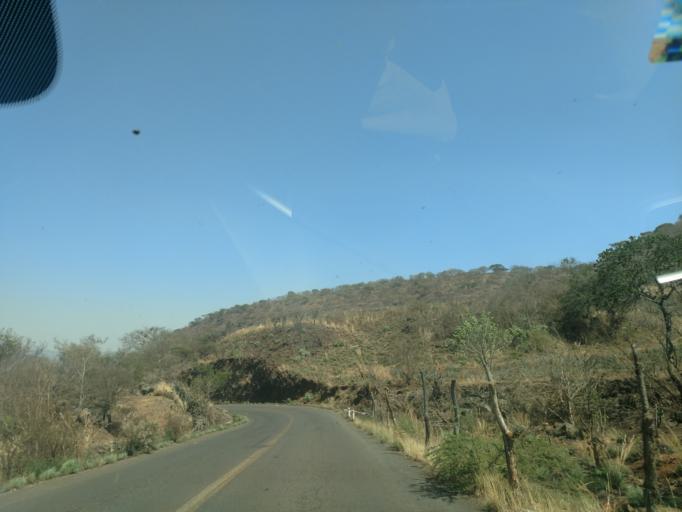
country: MX
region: Nayarit
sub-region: Tepic
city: La Corregidora
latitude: 21.4766
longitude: -104.6729
